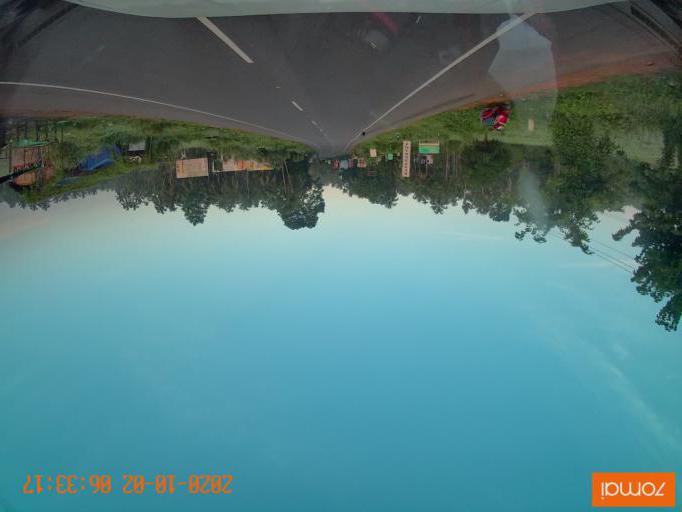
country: IN
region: Kerala
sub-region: Malappuram
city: Ponnani
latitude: 10.7587
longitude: 76.0166
